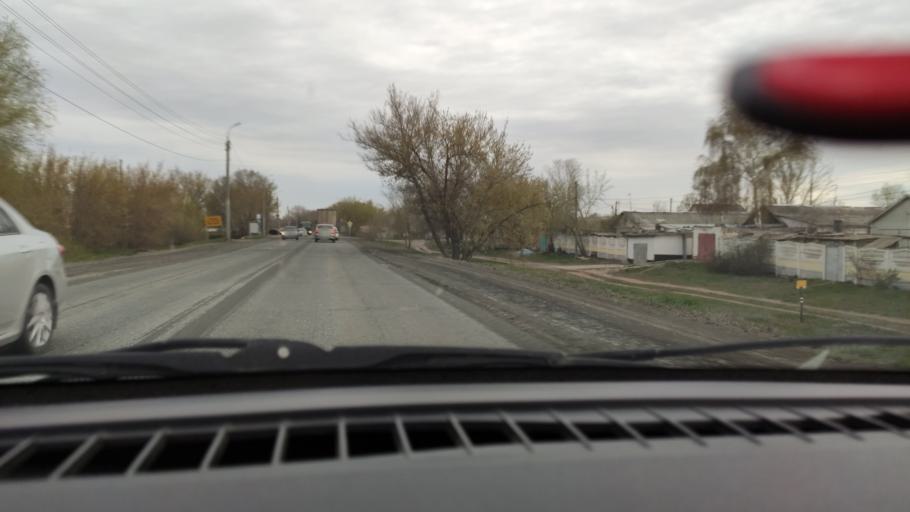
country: RU
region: Orenburg
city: Tatarskaya Kargala
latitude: 51.8618
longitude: 55.1358
